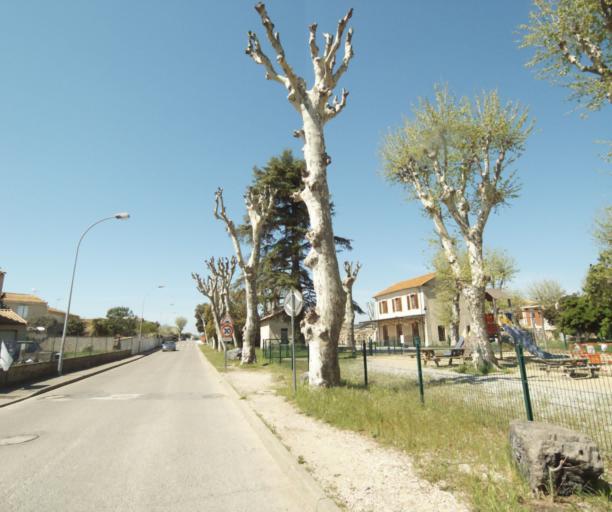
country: FR
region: Languedoc-Roussillon
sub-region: Departement de l'Herault
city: Castries
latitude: 43.6744
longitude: 3.9898
